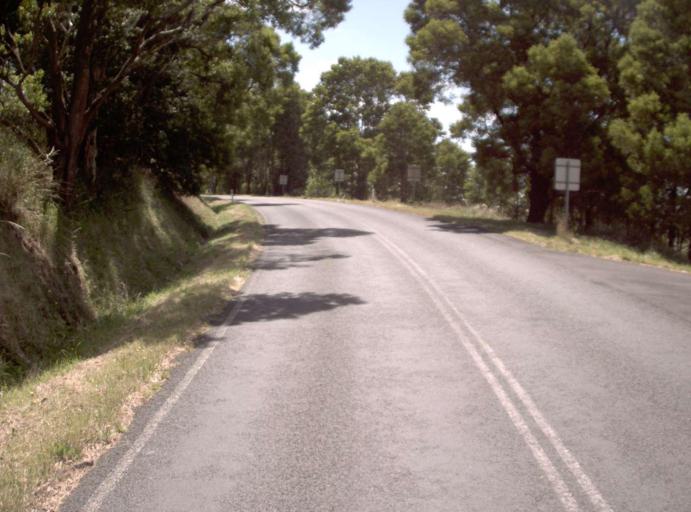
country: AU
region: Victoria
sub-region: Baw Baw
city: Warragul
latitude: -38.3650
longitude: 145.8601
